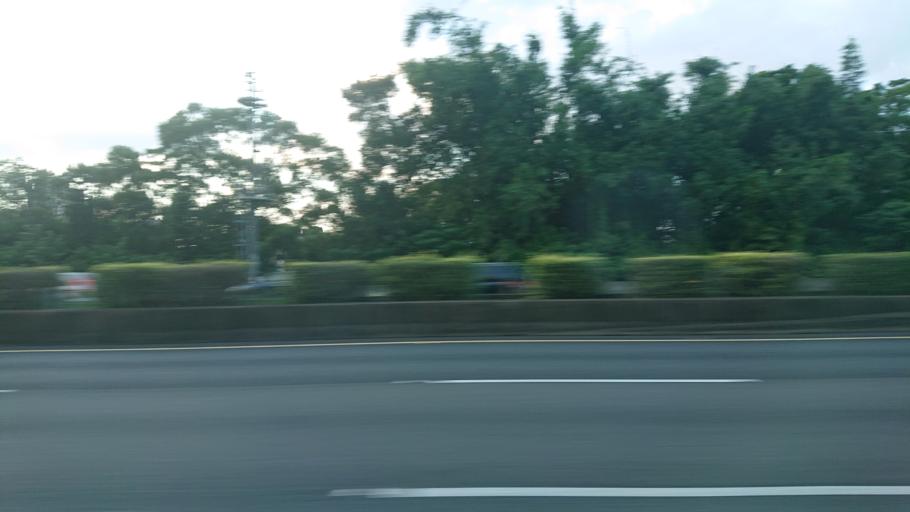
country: TW
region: Taipei
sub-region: Taipei
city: Banqiao
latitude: 24.9822
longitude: 121.4713
